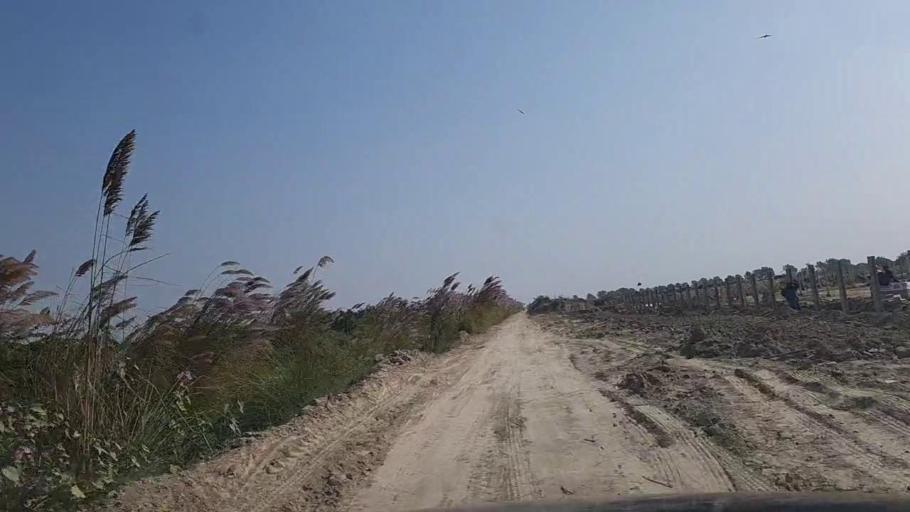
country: PK
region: Sindh
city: Gharo
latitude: 24.7177
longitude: 67.5655
